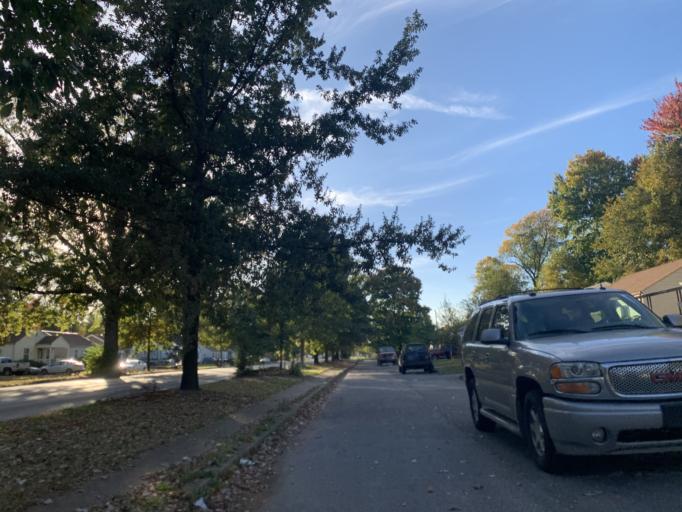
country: US
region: Kentucky
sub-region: Jefferson County
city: Shively
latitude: 38.2243
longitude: -85.8060
